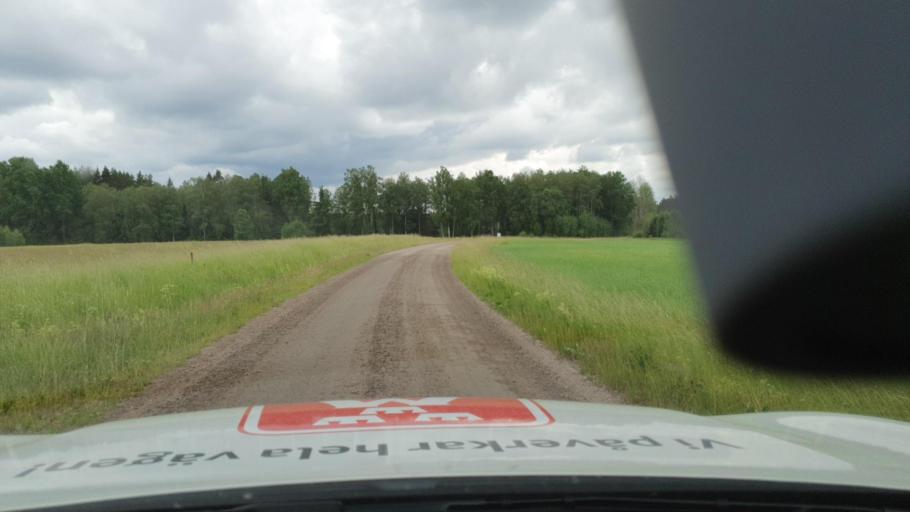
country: SE
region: Vaestra Goetaland
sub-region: Tidaholms Kommun
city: Olofstorp
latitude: 58.1679
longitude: 14.0788
